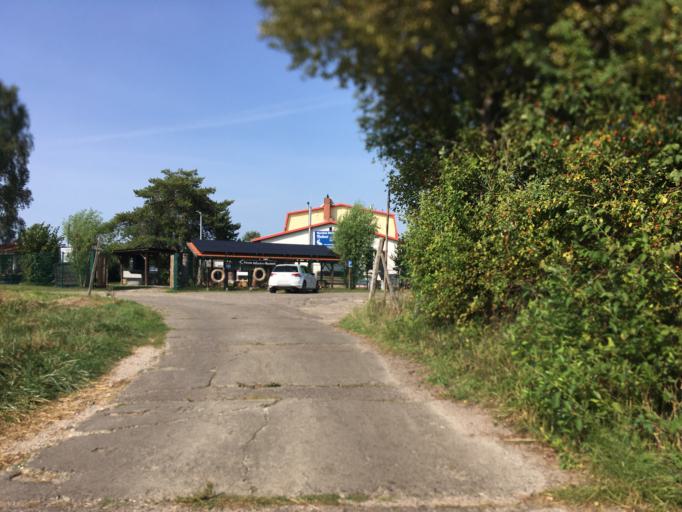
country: DE
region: Brandenburg
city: Erkner
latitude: 52.3971
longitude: 13.7333
